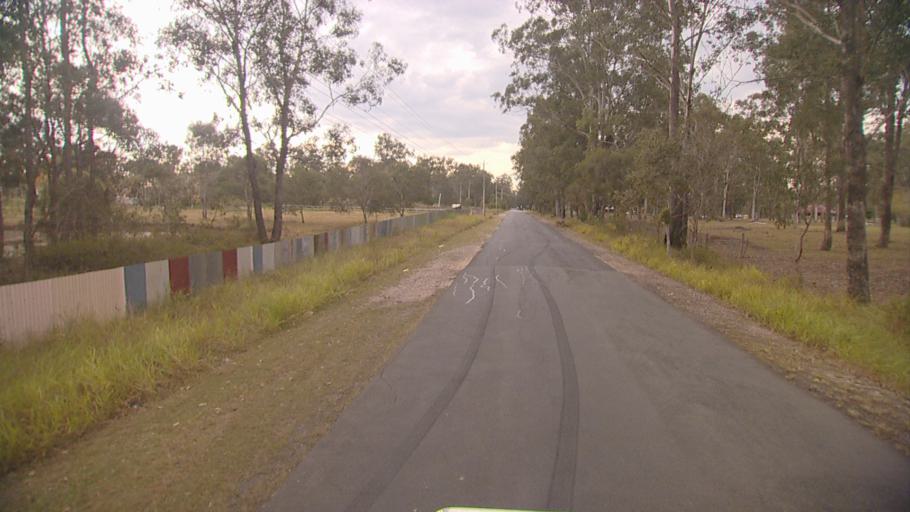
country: AU
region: Queensland
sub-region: Logan
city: Chambers Flat
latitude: -27.7726
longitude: 153.1157
